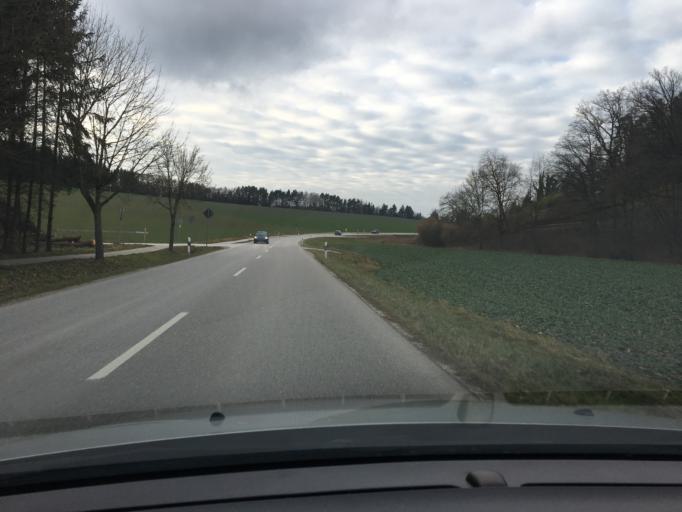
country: DE
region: Bavaria
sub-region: Lower Bavaria
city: Kumhausen
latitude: 48.5020
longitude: 12.1734
